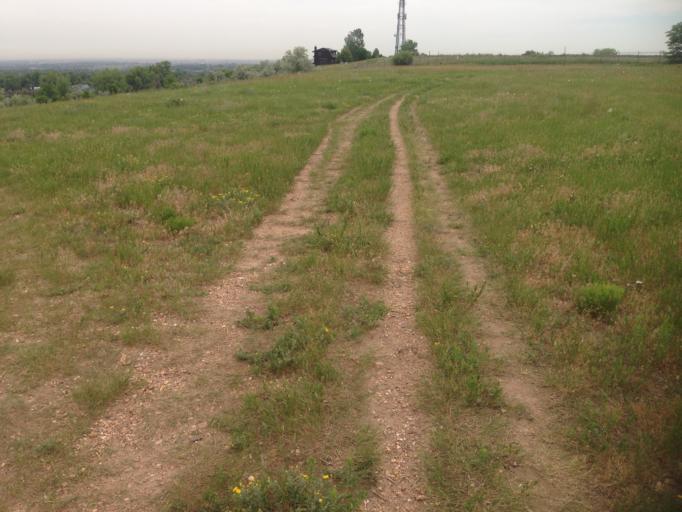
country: US
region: Colorado
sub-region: Boulder County
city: Louisville
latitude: 39.9918
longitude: -105.1592
